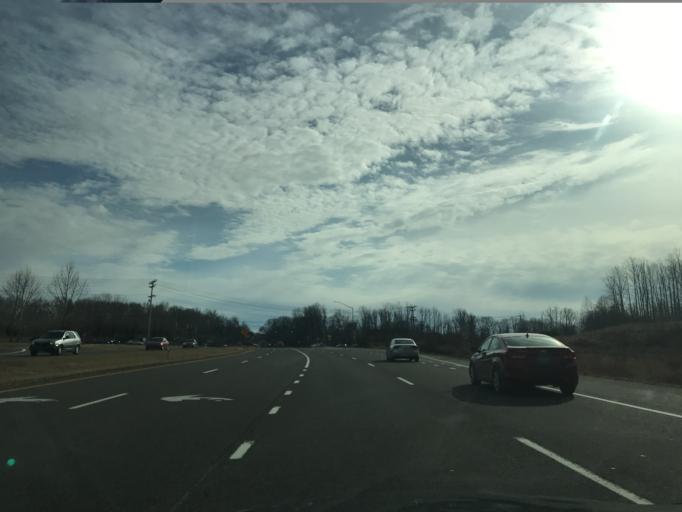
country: US
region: Maryland
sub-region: Prince George's County
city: Glenn Dale
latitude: 38.9632
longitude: -76.7976
